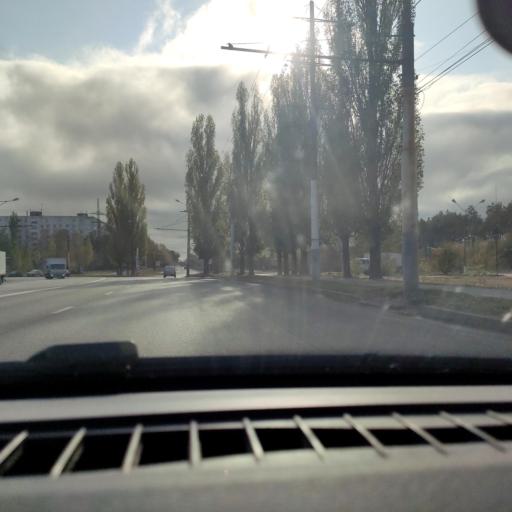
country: RU
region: Voronezj
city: Maslovka
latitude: 51.6033
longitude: 39.2369
